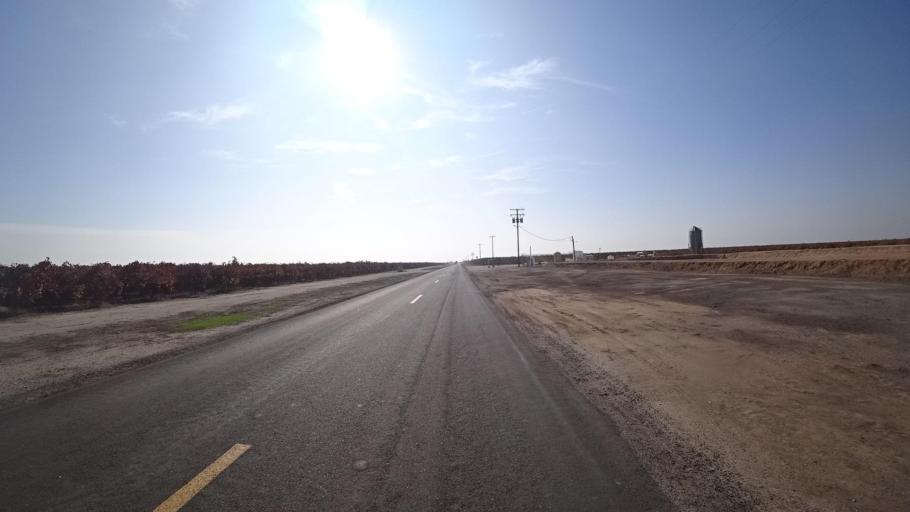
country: US
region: California
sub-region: Kern County
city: McFarland
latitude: 35.6868
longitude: -119.1692
